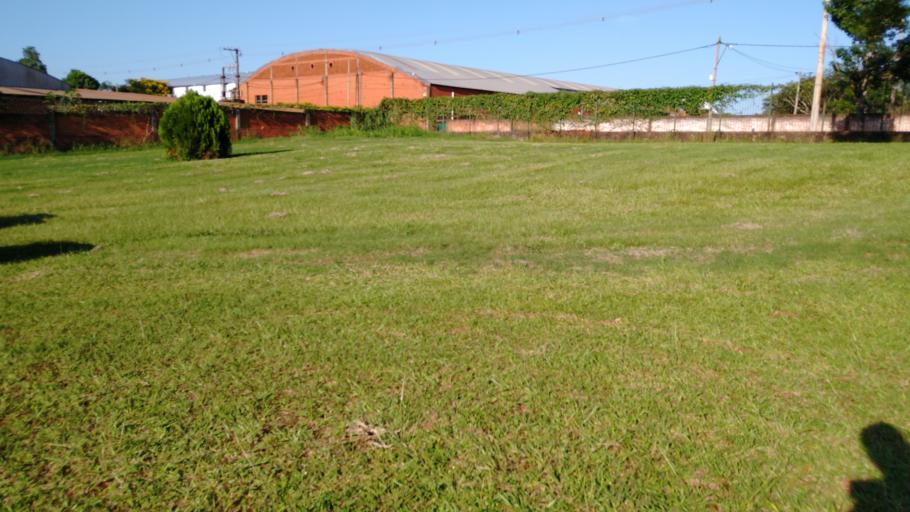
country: AR
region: Misiones
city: Puerto Rico
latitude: -26.8048
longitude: -55.0280
